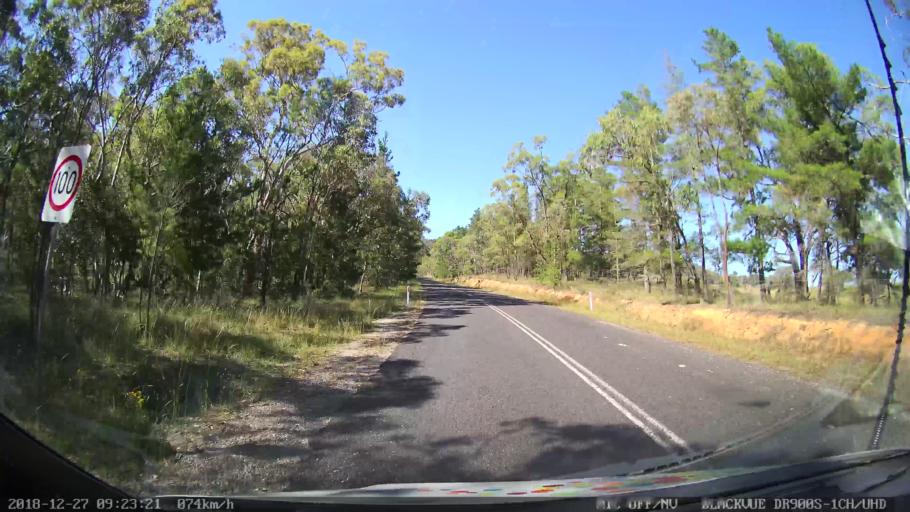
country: AU
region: New South Wales
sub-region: Lithgow
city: Portland
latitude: -33.1251
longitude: 149.9979
